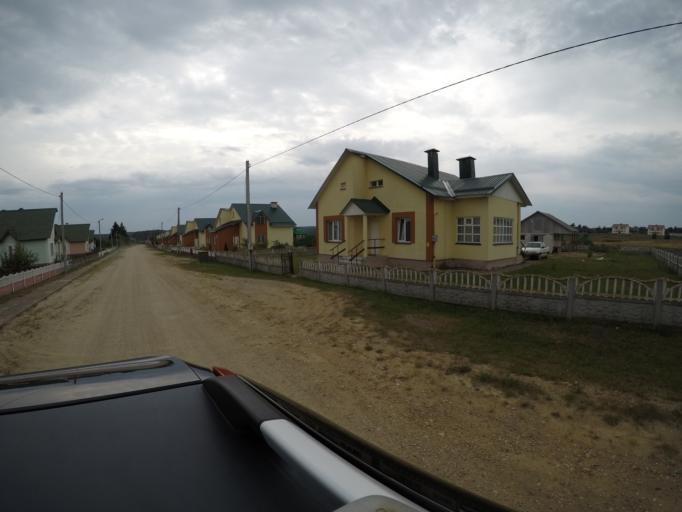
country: BY
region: Grodnenskaya
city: Hal'shany
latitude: 54.2565
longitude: 26.0251
